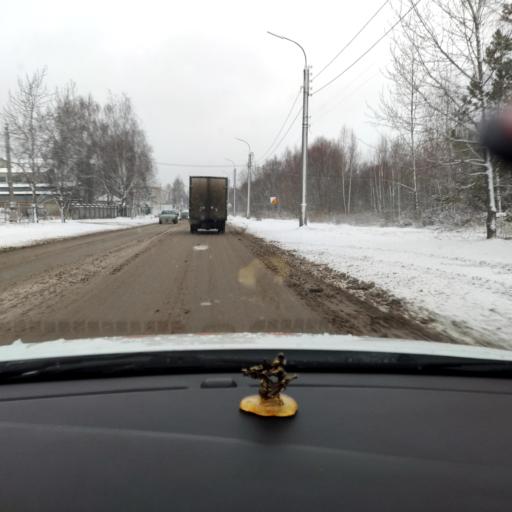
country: RU
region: Tatarstan
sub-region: Zelenodol'skiy Rayon
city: Zelenodolsk
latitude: 55.8630
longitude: 48.5496
